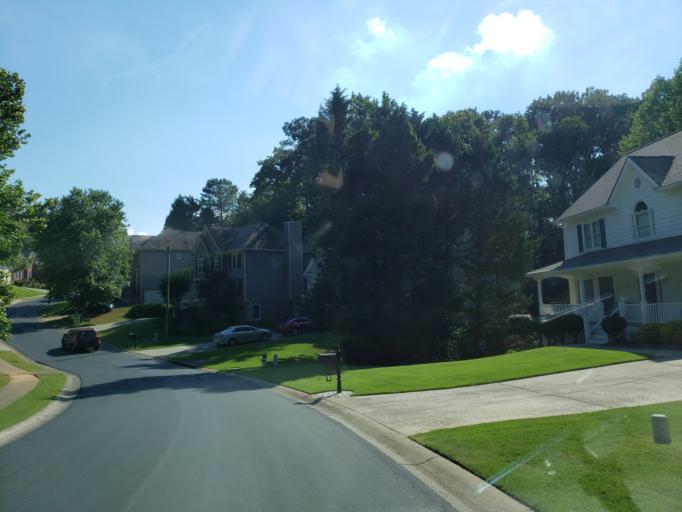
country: US
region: Georgia
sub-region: Cherokee County
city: Woodstock
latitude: 34.1206
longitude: -84.5357
